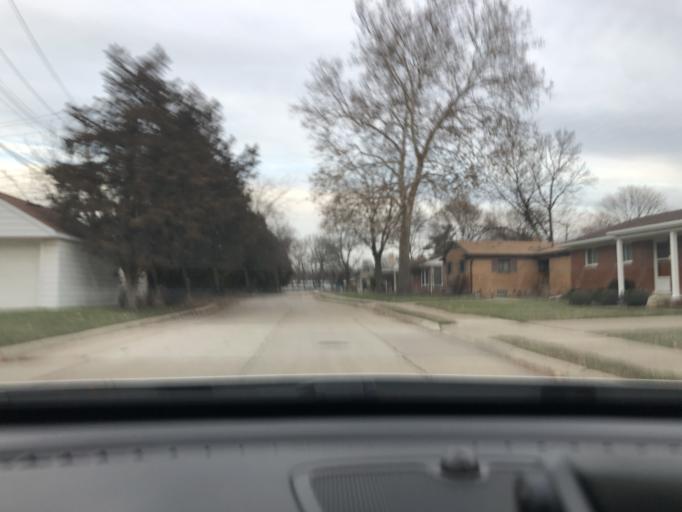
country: US
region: Michigan
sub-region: Wayne County
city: Allen Park
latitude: 42.2848
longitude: -83.2245
